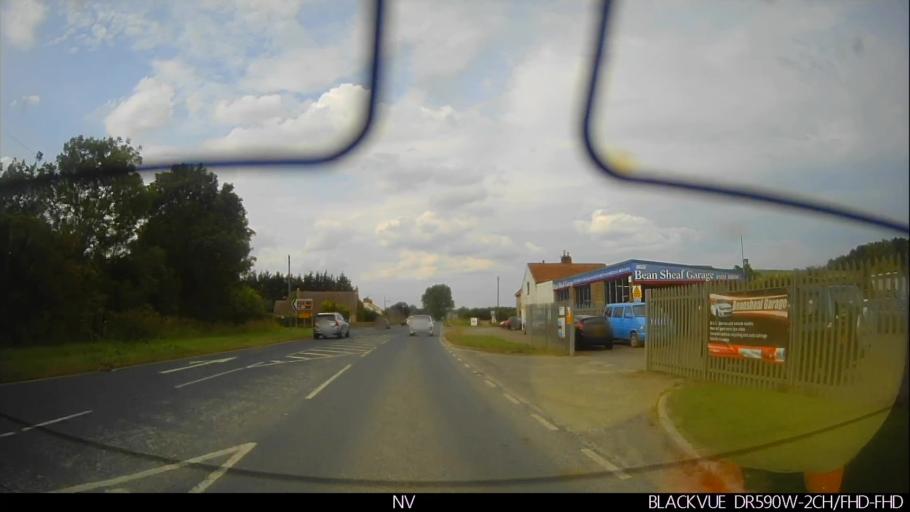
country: GB
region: England
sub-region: North Yorkshire
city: Marishes
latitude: 54.2106
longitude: -0.7715
